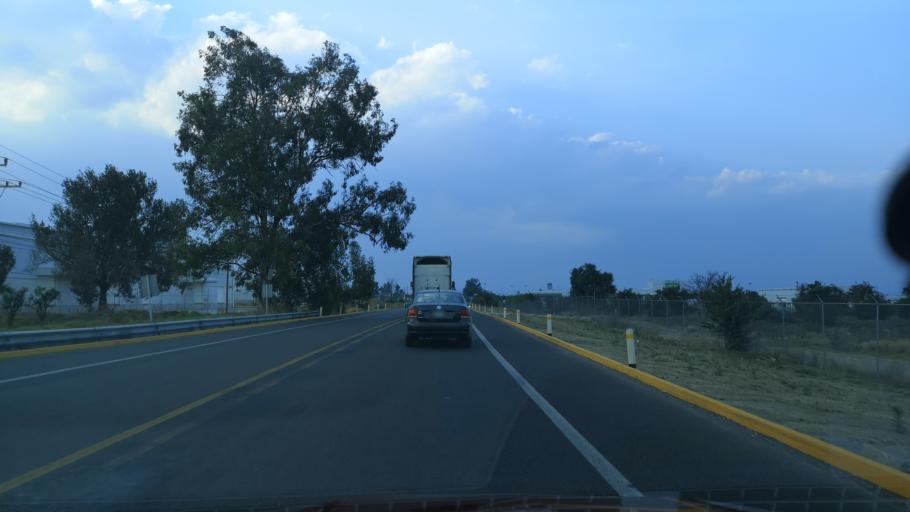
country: MX
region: Puebla
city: Huejotzingo
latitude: 19.1544
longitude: -98.3771
